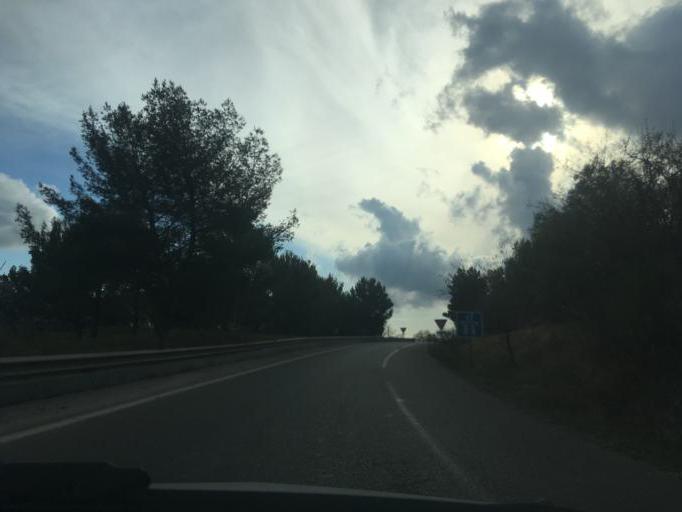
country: FR
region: Provence-Alpes-Cote d'Azur
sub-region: Departement du Var
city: Cuers
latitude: 43.2238
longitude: 6.0702
